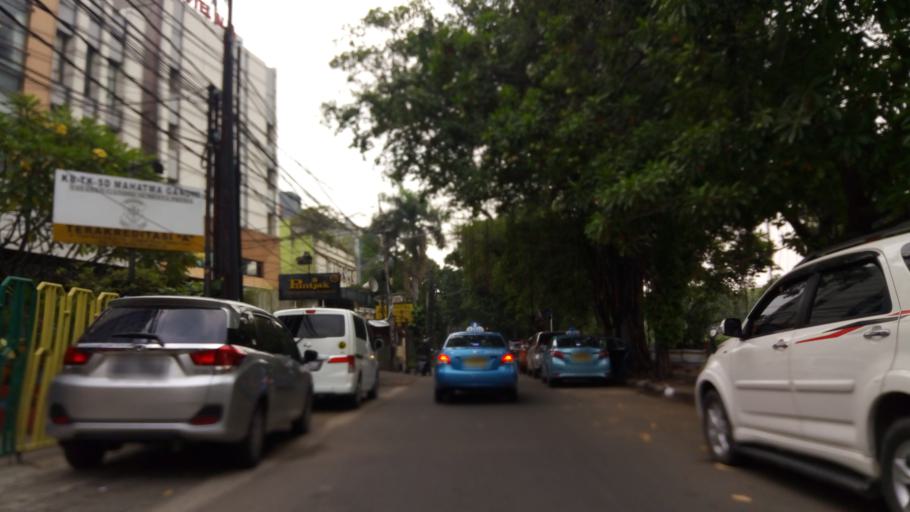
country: ID
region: Jakarta Raya
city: Jakarta
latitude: -6.1650
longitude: 106.8356
